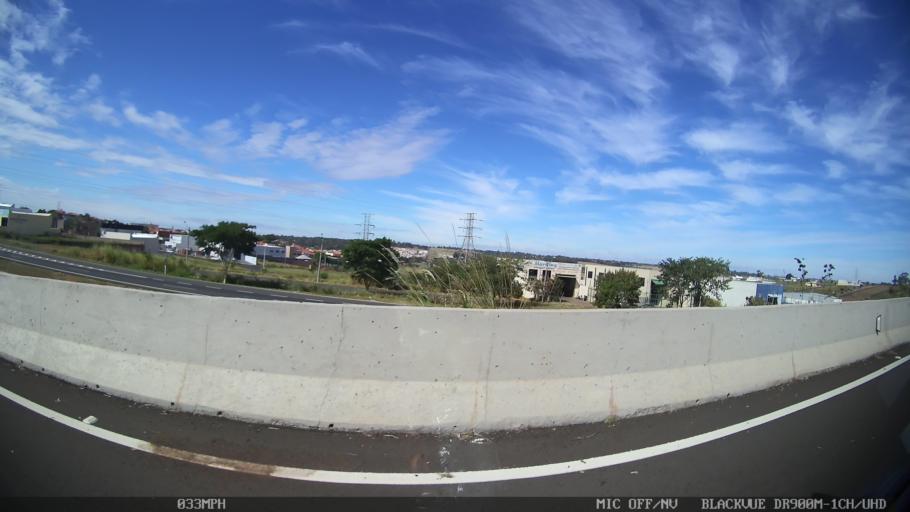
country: BR
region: Sao Paulo
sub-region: Sao Jose Do Rio Preto
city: Sao Jose do Rio Preto
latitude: -20.8449
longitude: -49.3732
